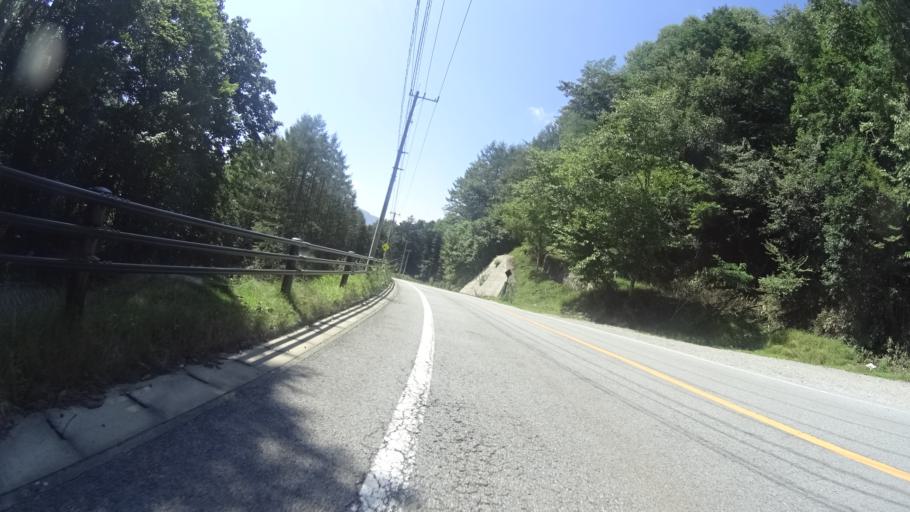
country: JP
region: Yamanashi
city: Enzan
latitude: 35.7696
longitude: 138.8035
